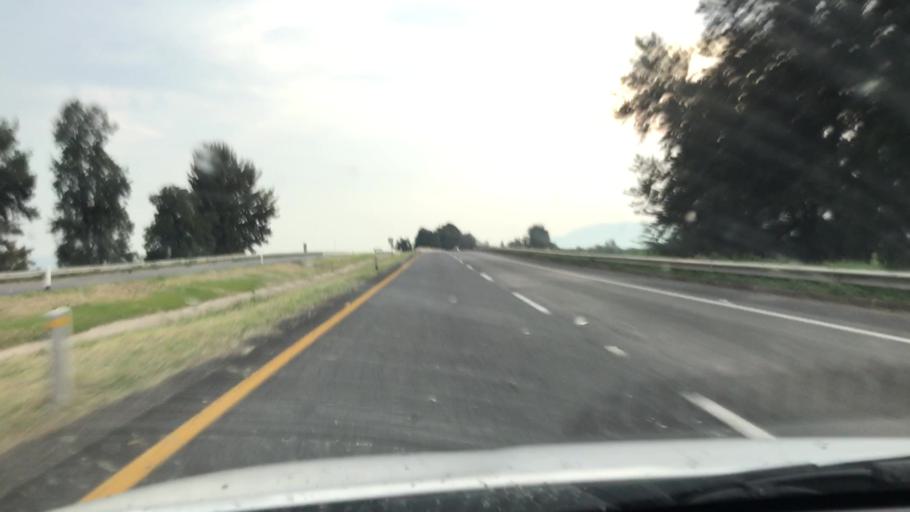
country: MX
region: Michoacan
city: Vistahermosa de Negrete
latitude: 20.2905
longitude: -102.4708
